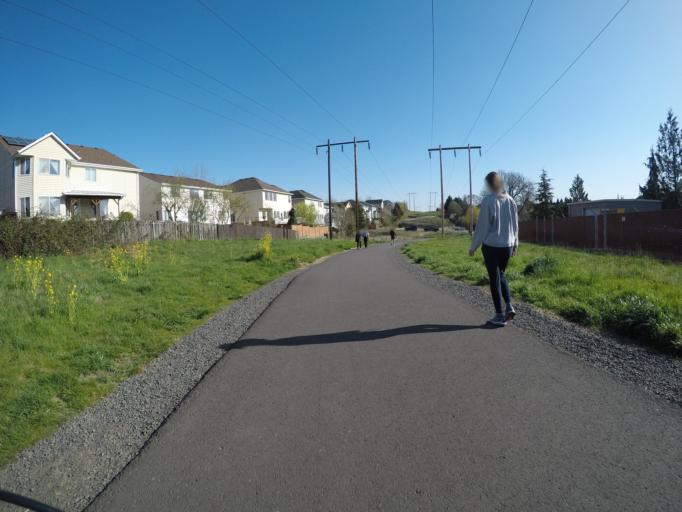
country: US
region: Oregon
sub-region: Washington County
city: Oak Hills
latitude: 45.5607
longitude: -122.8261
